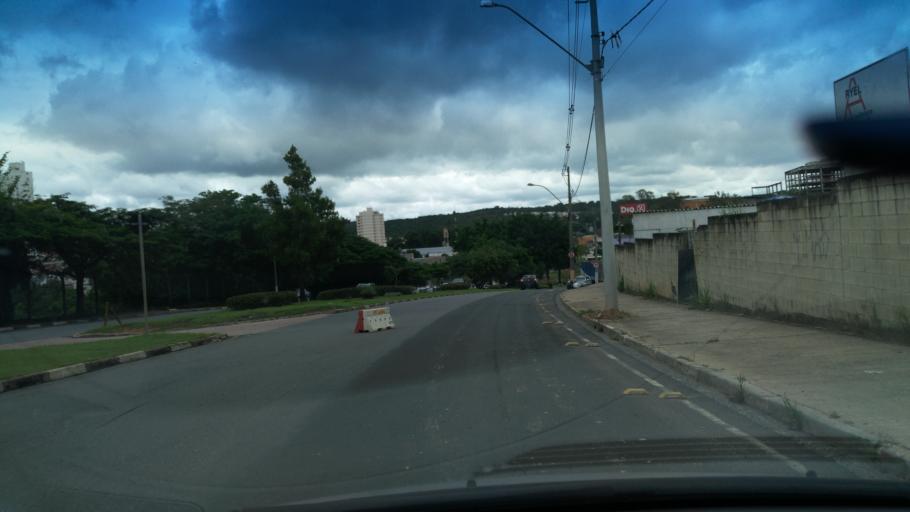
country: BR
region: Sao Paulo
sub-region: Valinhos
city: Valinhos
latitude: -22.9636
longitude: -46.9985
